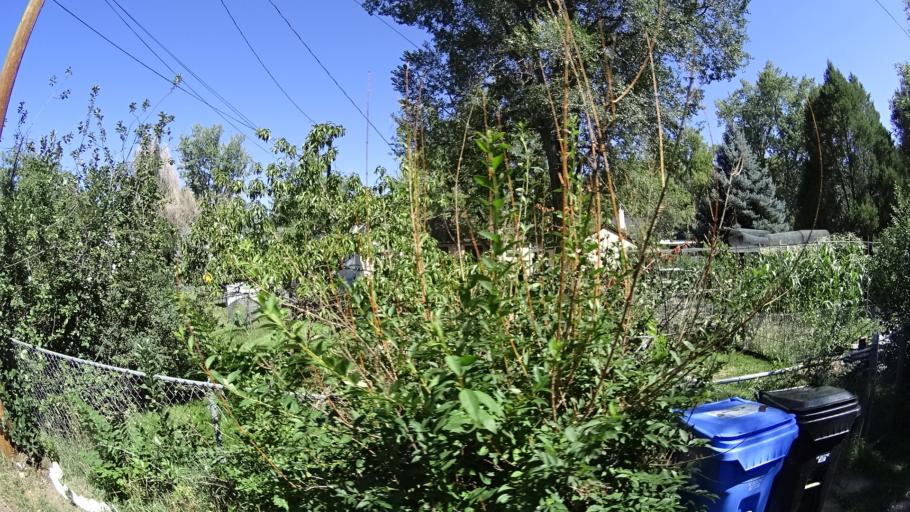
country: US
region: Colorado
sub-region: El Paso County
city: Colorado Springs
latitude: 38.8411
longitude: -104.8026
